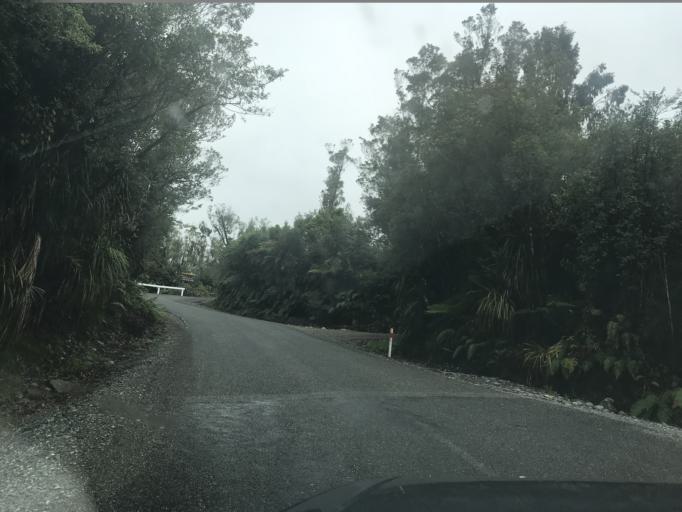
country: NZ
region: West Coast
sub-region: Westland District
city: Hokitika
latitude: -42.9560
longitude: 171.0200
